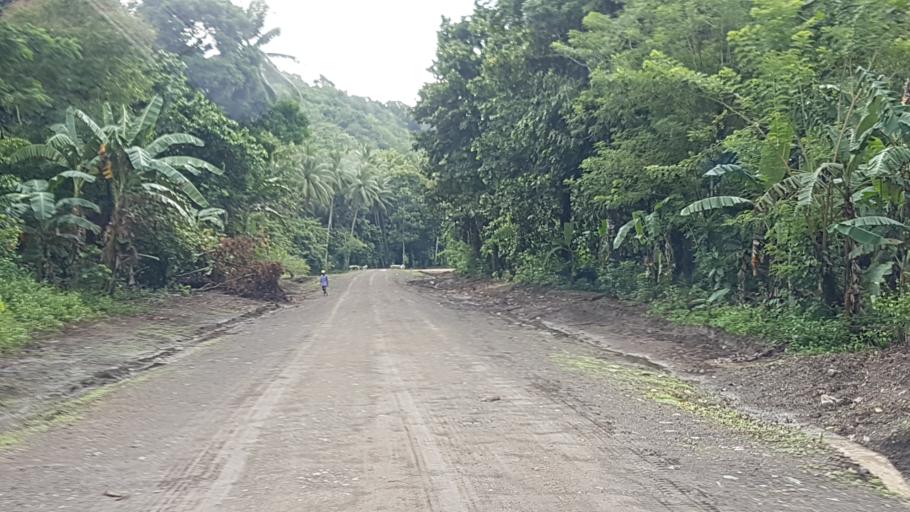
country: PG
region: Milne Bay
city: Alotau
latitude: -10.2958
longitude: 150.7333
